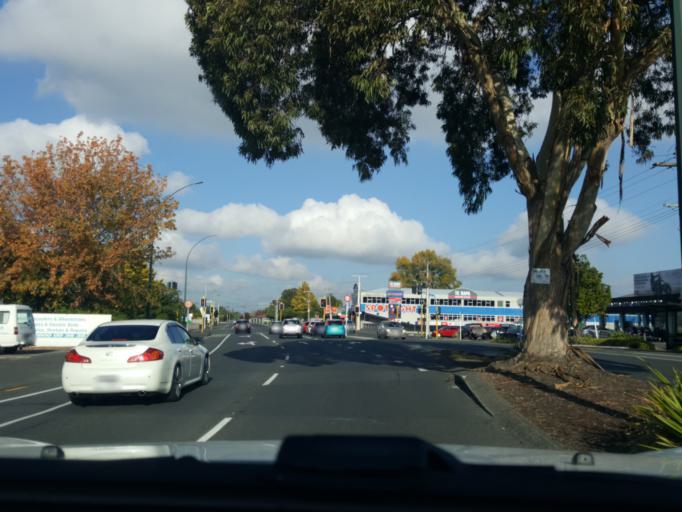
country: NZ
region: Waikato
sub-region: Hamilton City
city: Hamilton
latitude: -37.7640
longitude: 175.2524
